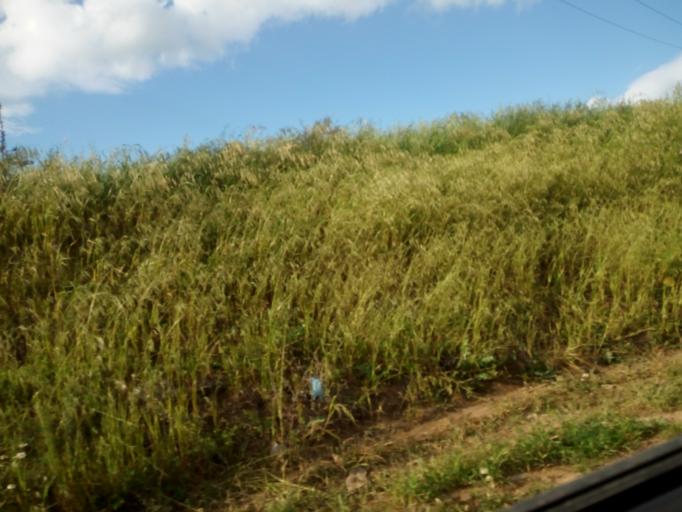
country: DZ
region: Tipaza
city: Hadjout
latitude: 36.3739
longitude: 2.4948
